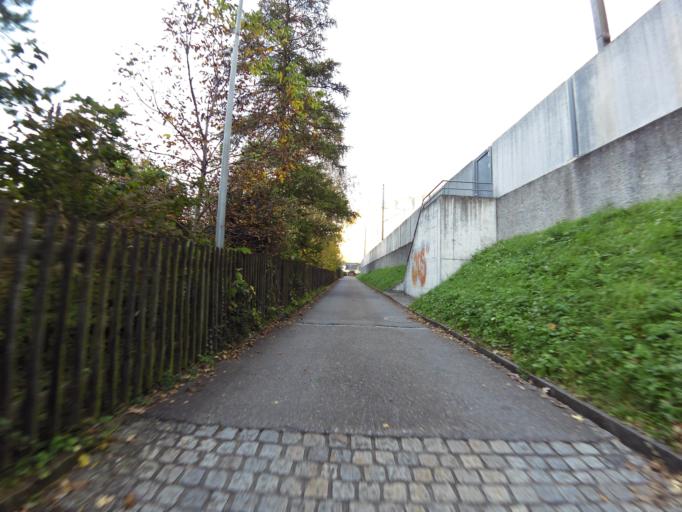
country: CH
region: Uri
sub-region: Uri
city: Flueelen
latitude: 46.9103
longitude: 8.6221
